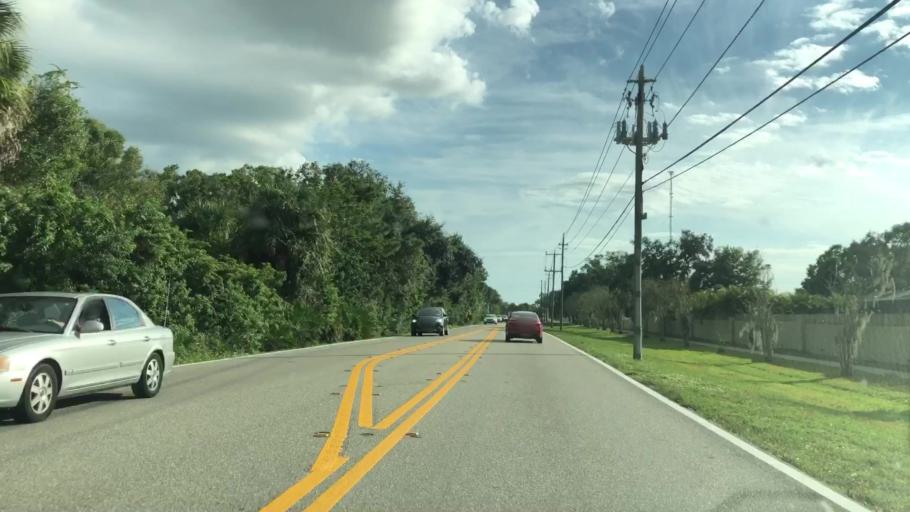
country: US
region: Florida
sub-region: Sarasota County
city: The Meadows
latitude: 27.3472
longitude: -82.4639
